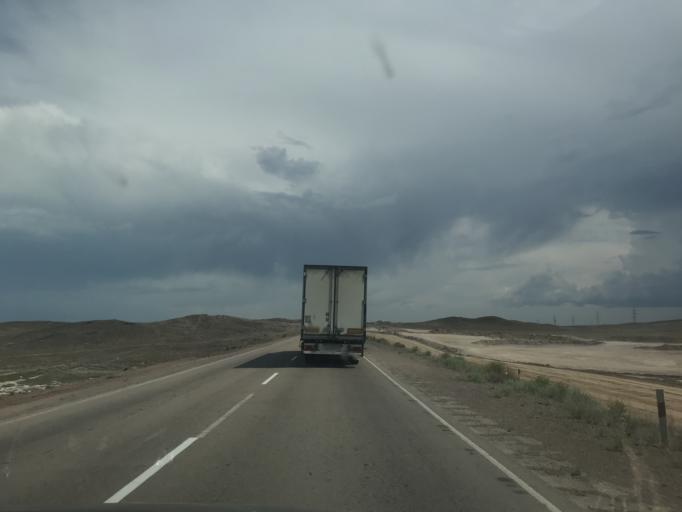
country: KZ
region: Zhambyl
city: Mynaral
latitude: 45.3061
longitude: 73.7580
